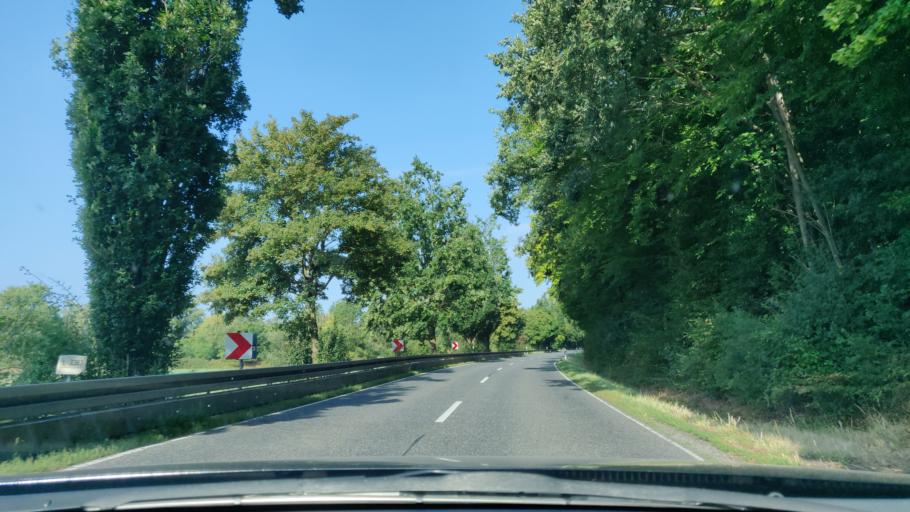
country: DE
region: Hesse
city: Fritzlar
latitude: 51.1295
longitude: 9.2202
